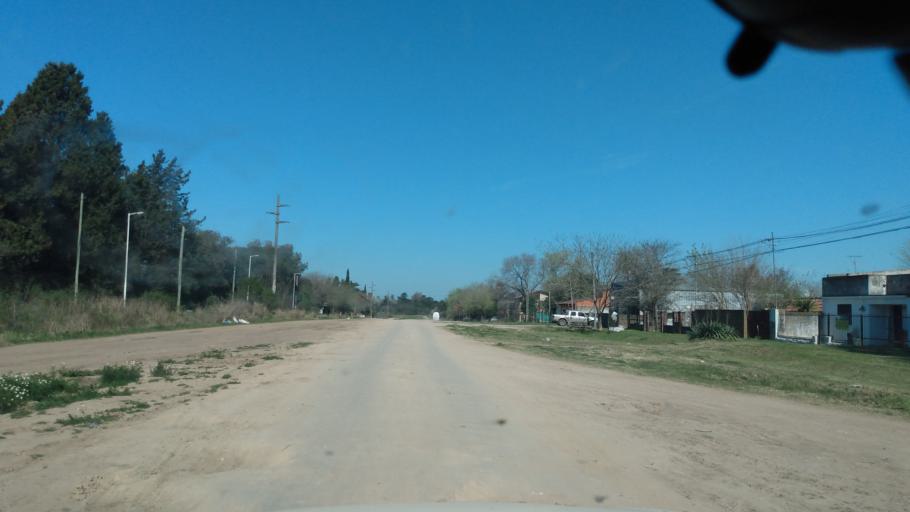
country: AR
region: Buenos Aires
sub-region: Partido de Lujan
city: Lujan
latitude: -34.5712
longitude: -59.1363
